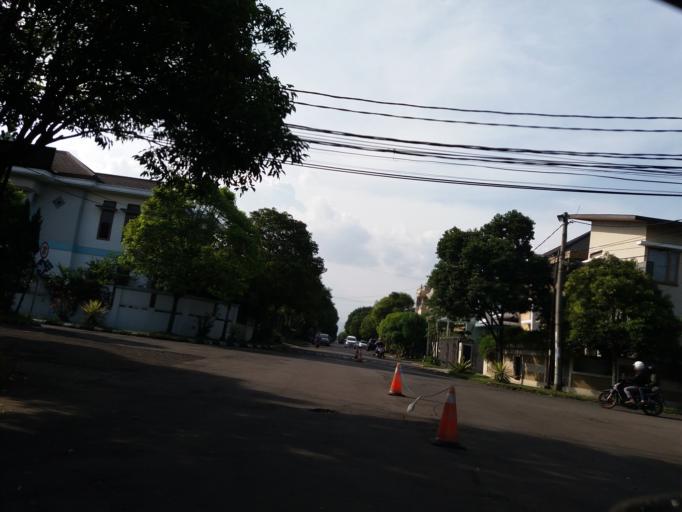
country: ID
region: West Java
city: Bandung
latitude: -6.9623
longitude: 107.6298
